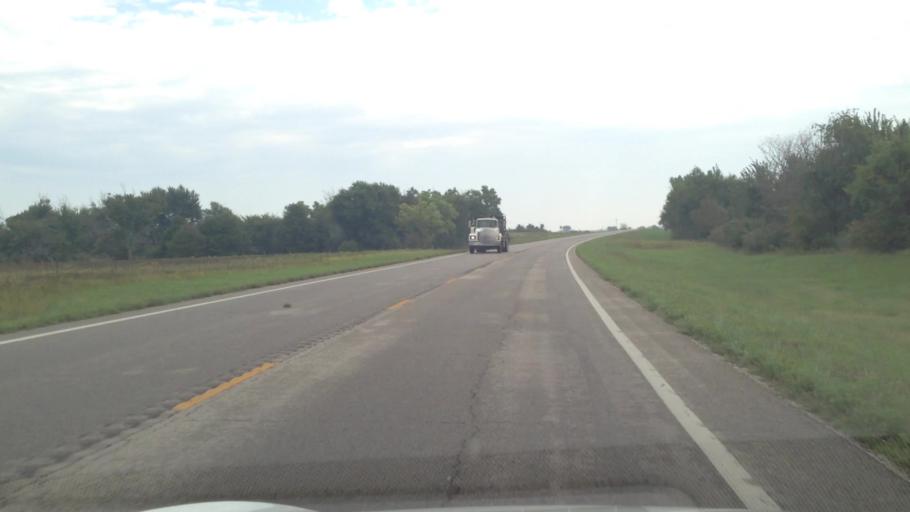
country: US
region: Kansas
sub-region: Bourbon County
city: Fort Scott
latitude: 37.8912
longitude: -95.0380
